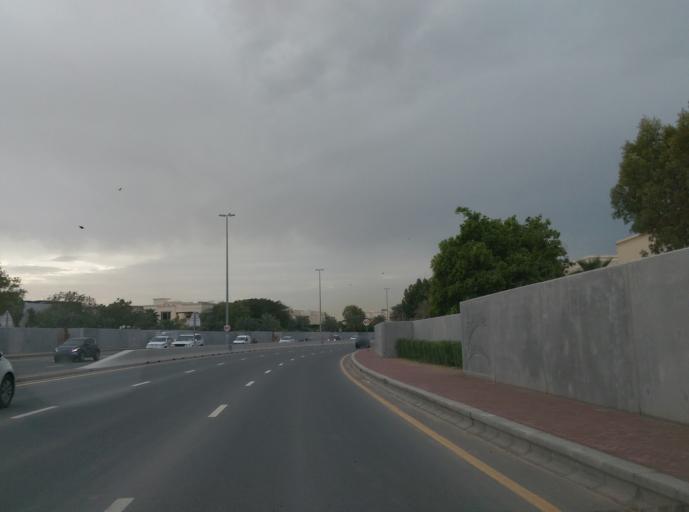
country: AE
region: Dubai
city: Dubai
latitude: 25.0766
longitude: 55.1757
